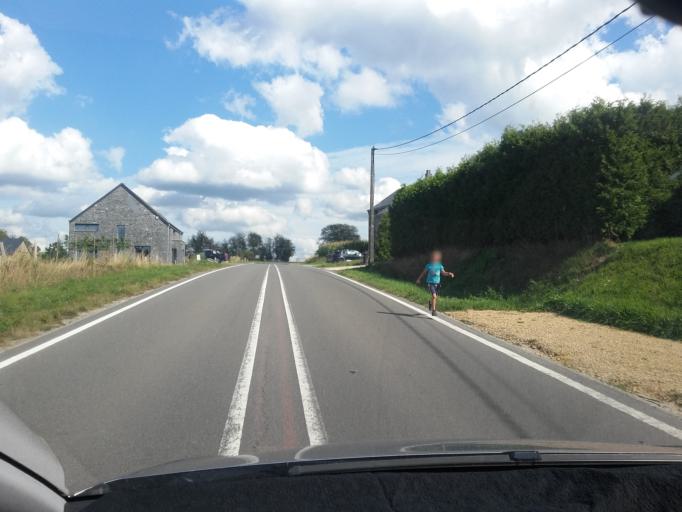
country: BE
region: Wallonia
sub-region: Province du Luxembourg
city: Saint-Hubert
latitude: 50.0317
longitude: 5.3272
